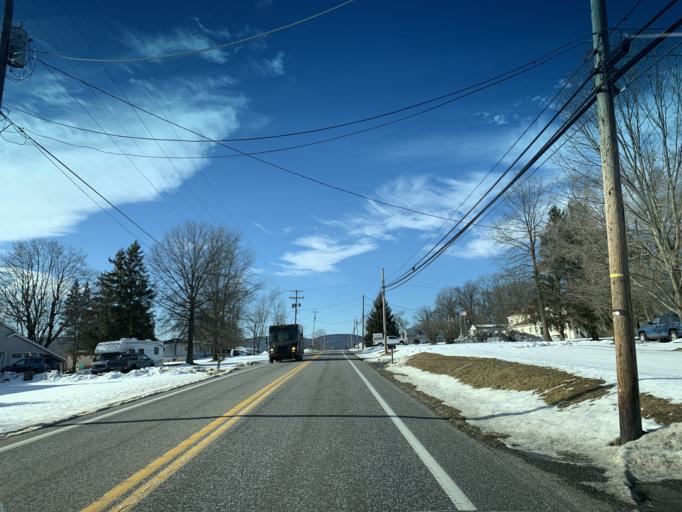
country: US
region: Pennsylvania
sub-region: York County
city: Dillsburg
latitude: 40.0889
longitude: -77.0233
